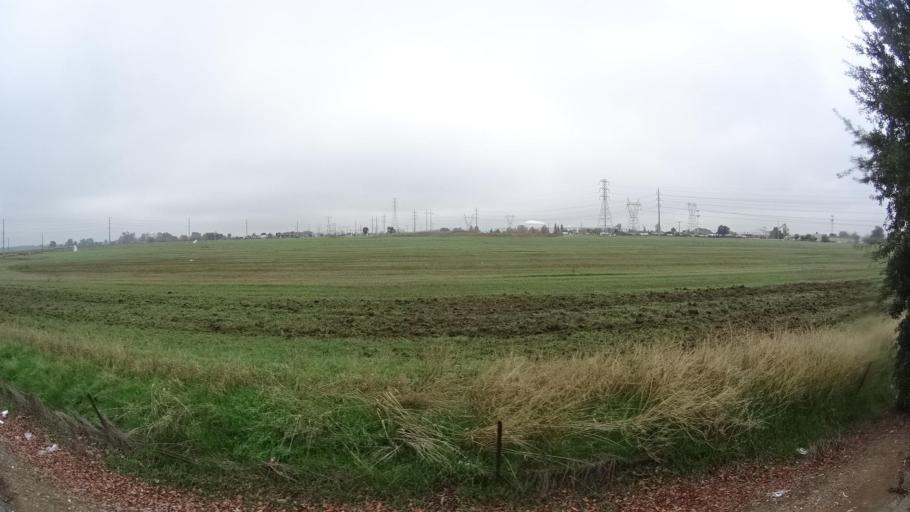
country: US
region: California
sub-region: Sacramento County
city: Elk Grove
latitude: 38.3898
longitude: -121.3485
